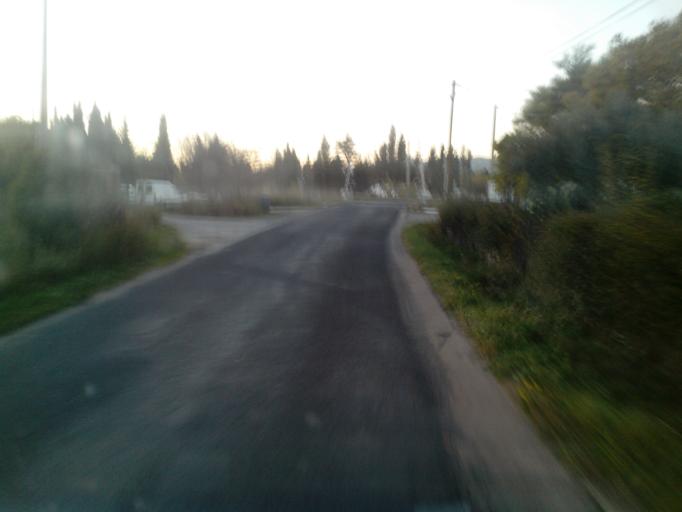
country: FR
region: Languedoc-Roussillon
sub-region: Departement des Pyrenees-Orientales
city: Rivesaltes
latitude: 42.7712
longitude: 2.8571
